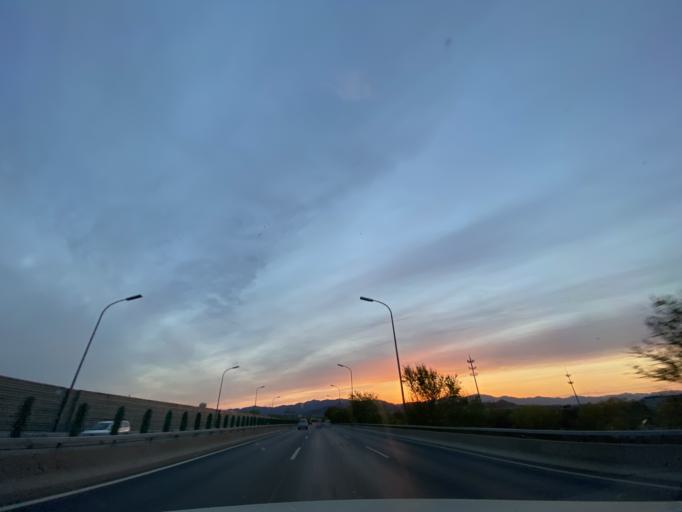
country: CN
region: Beijing
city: Qinghe
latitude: 40.0168
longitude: 116.3085
